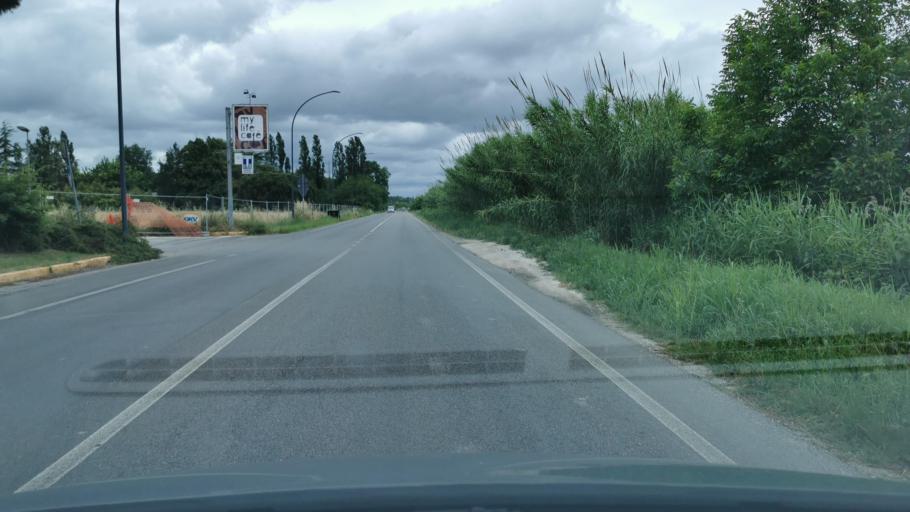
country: IT
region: Emilia-Romagna
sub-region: Provincia di Ravenna
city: Madonna Dell'Albero
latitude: 44.3865
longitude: 12.1960
